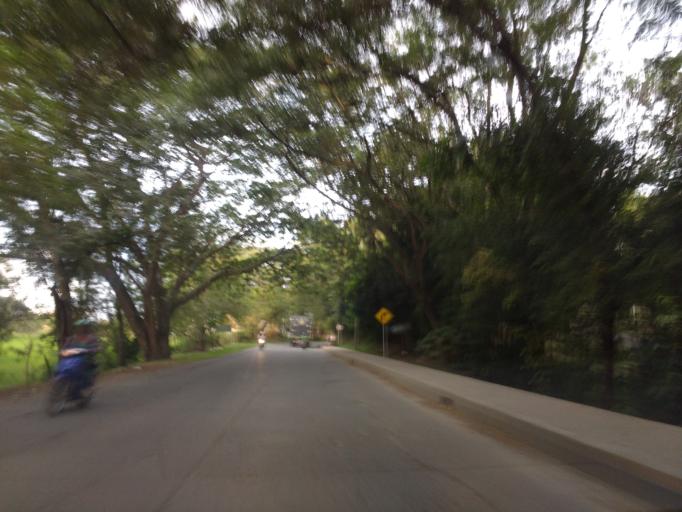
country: CO
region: Valle del Cauca
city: Cartago
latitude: 4.7535
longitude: -75.9331
